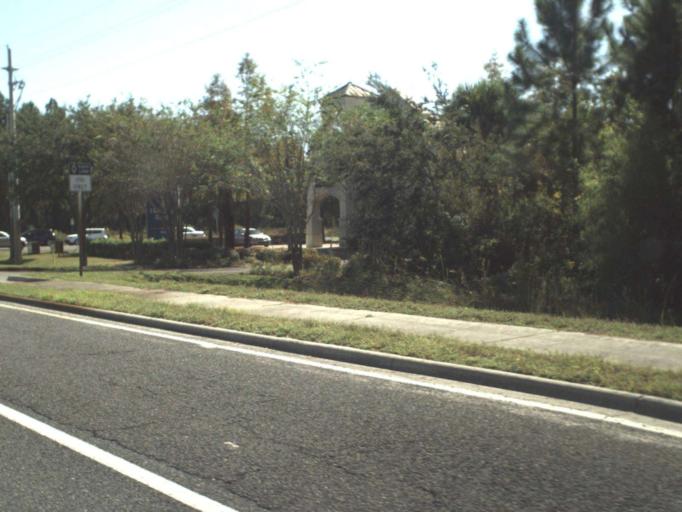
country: US
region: Florida
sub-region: Walton County
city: Seaside
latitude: 30.3739
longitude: -86.2299
